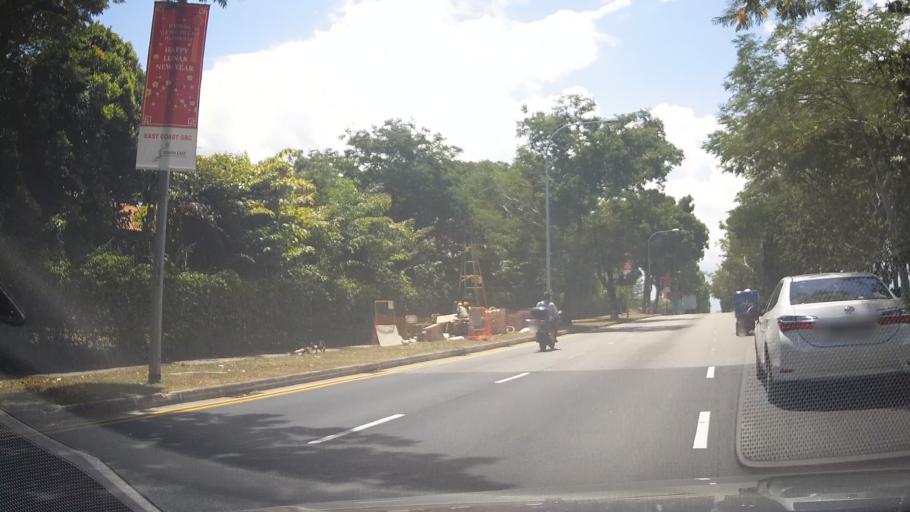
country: MY
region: Johor
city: Kampung Pasir Gudang Baru
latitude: 1.3686
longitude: 103.9695
